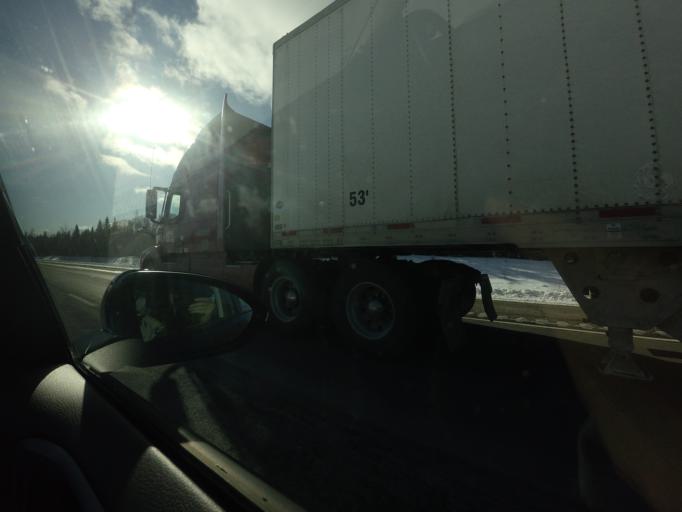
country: CA
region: New Brunswick
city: Fredericton
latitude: 45.8790
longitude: -66.6353
